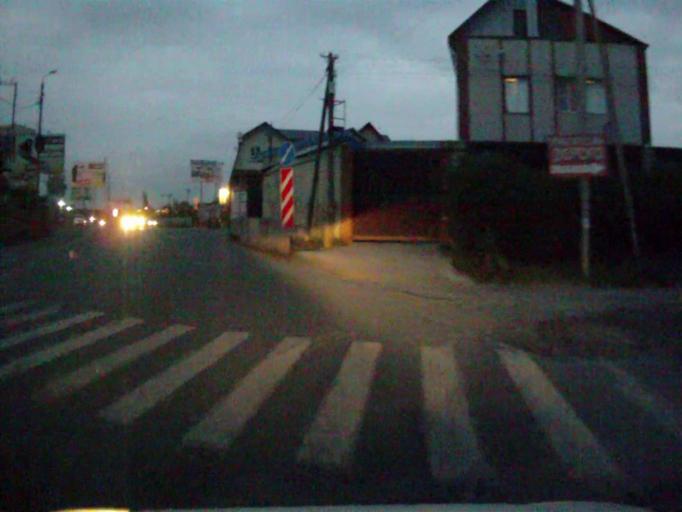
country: RU
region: Chelyabinsk
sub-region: Gorod Chelyabinsk
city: Chelyabinsk
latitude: 55.1549
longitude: 61.3021
